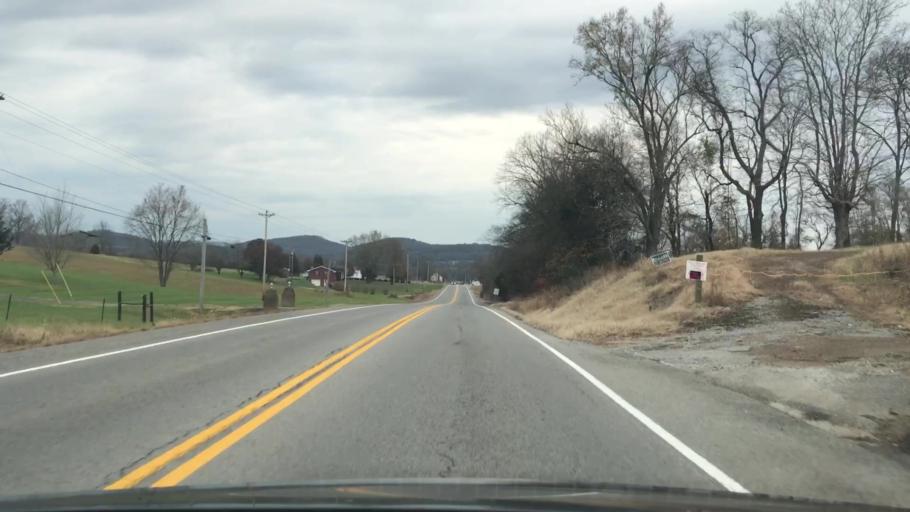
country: US
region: Tennessee
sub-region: Trousdale County
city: Hartsville
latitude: 36.3865
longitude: -86.1137
